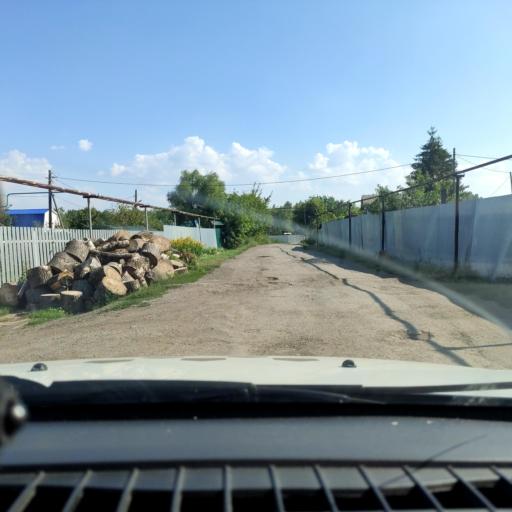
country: RU
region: Samara
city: Smyshlyayevka
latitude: 53.2077
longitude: 50.3285
